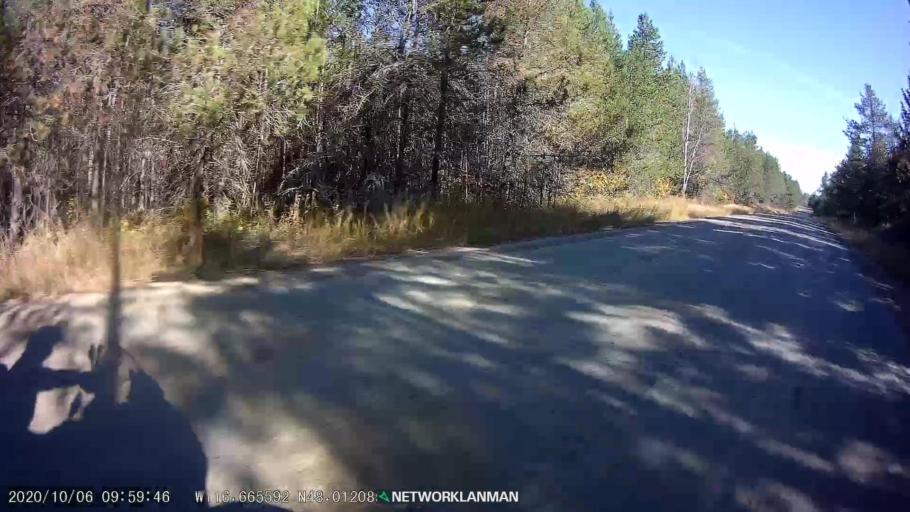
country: US
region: Idaho
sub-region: Kootenai County
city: Spirit Lake
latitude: 48.0122
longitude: -116.6653
